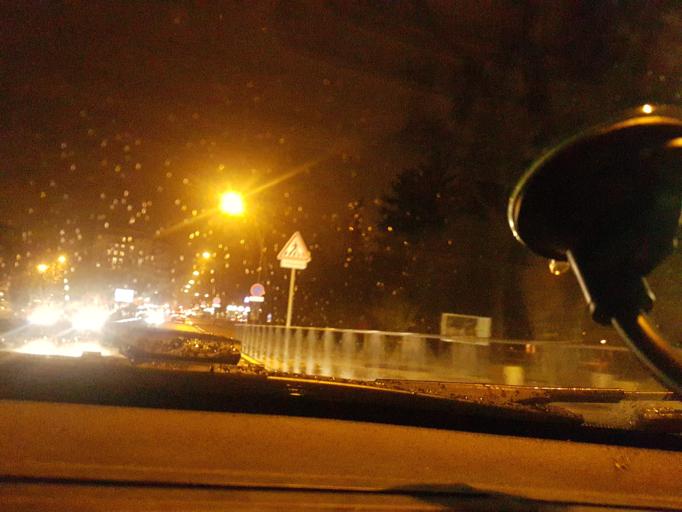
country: FR
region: Bourgogne
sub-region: Departement de Saone-et-Loire
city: Chalon-sur-Saone
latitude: 46.7838
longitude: 4.8604
